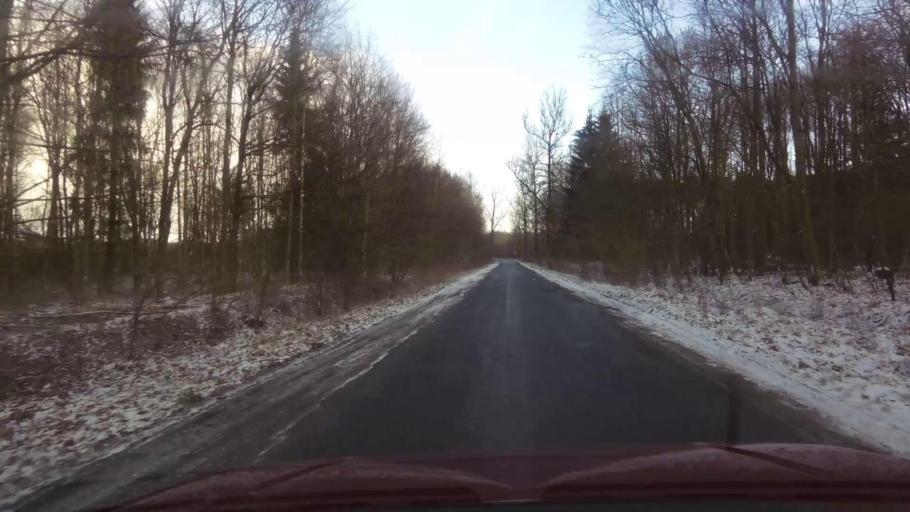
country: PL
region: West Pomeranian Voivodeship
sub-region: Powiat bialogardzki
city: Bialogard
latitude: 54.1049
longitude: 16.0118
